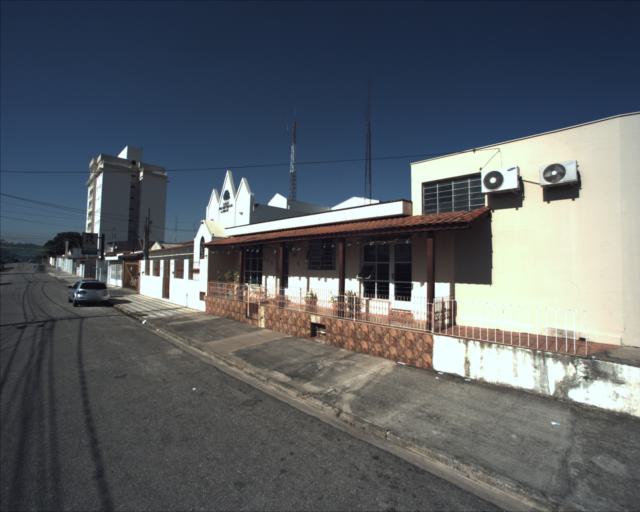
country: BR
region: Sao Paulo
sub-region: Sorocaba
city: Sorocaba
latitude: -23.5093
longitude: -47.4353
